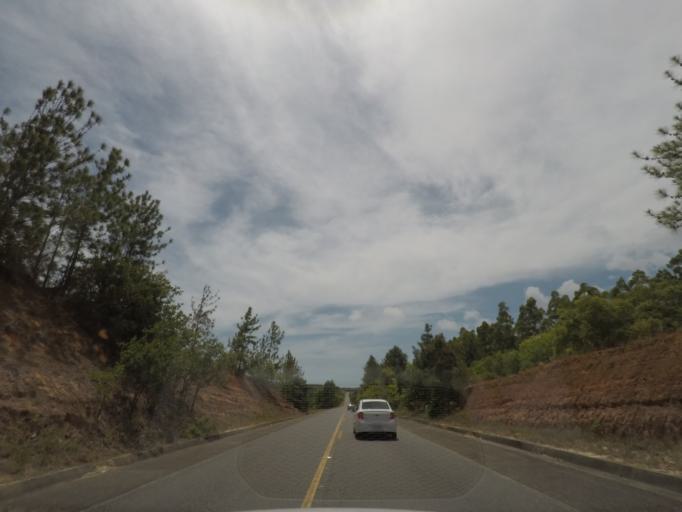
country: BR
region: Bahia
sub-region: Conde
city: Conde
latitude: -12.0088
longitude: -37.6866
